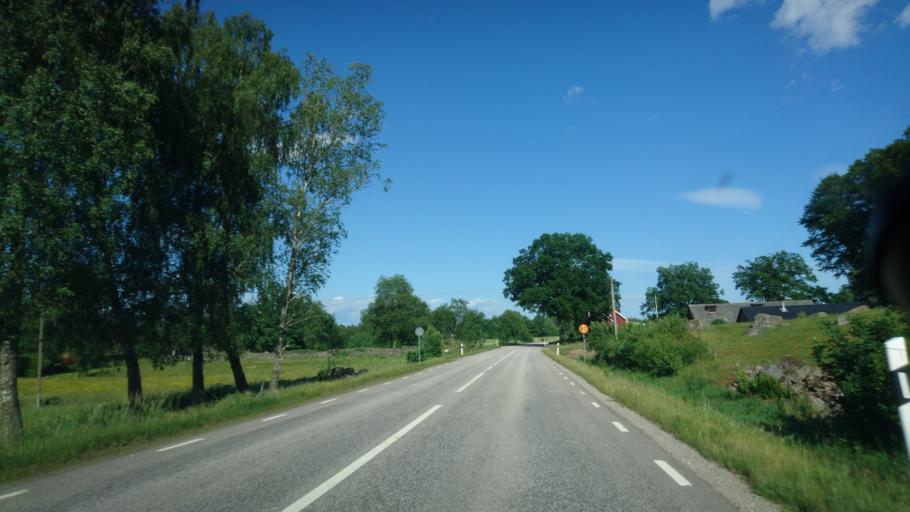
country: SE
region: Skane
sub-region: Osby Kommun
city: Lonsboda
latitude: 56.3915
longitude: 14.4470
